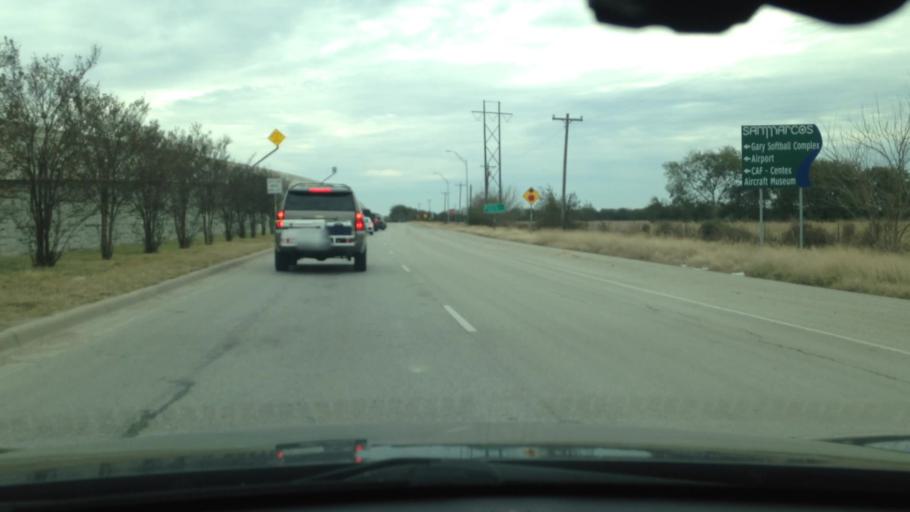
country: US
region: Texas
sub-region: Hays County
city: San Marcos
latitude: 29.8779
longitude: -97.9076
